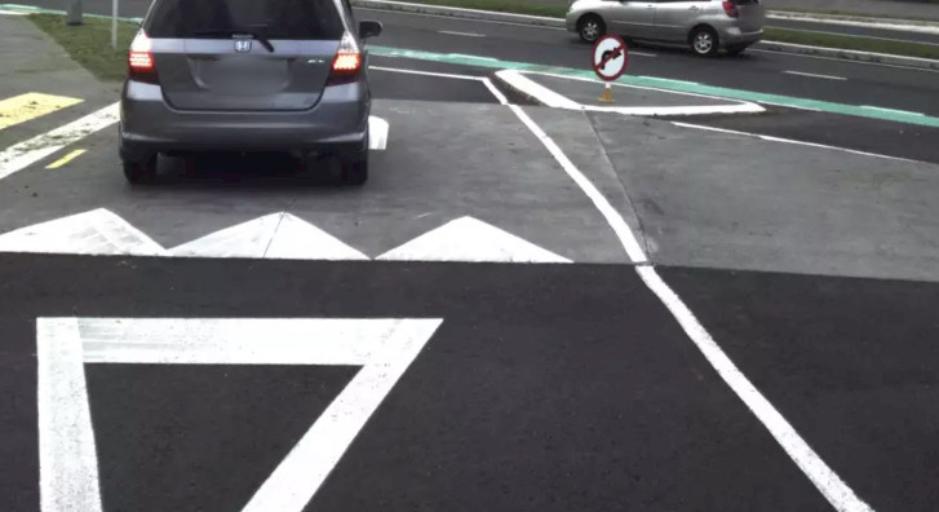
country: NZ
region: Auckland
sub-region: Auckland
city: Rothesay Bay
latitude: -36.7525
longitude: 174.6956
